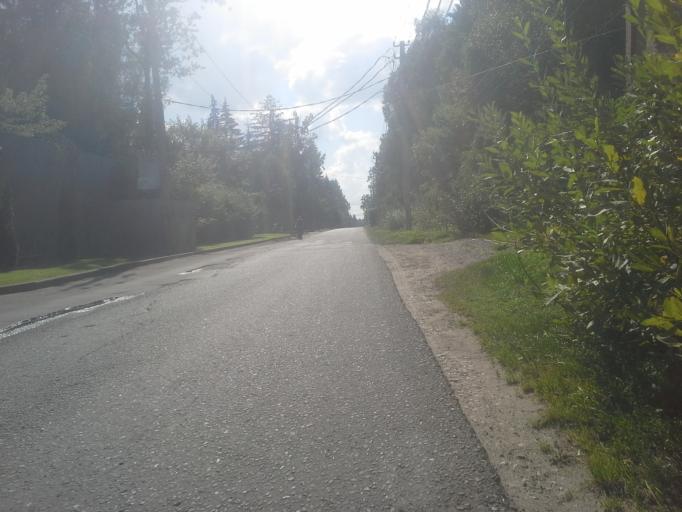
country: RU
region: Moskovskaya
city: Selyatino
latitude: 55.4724
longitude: 37.0070
